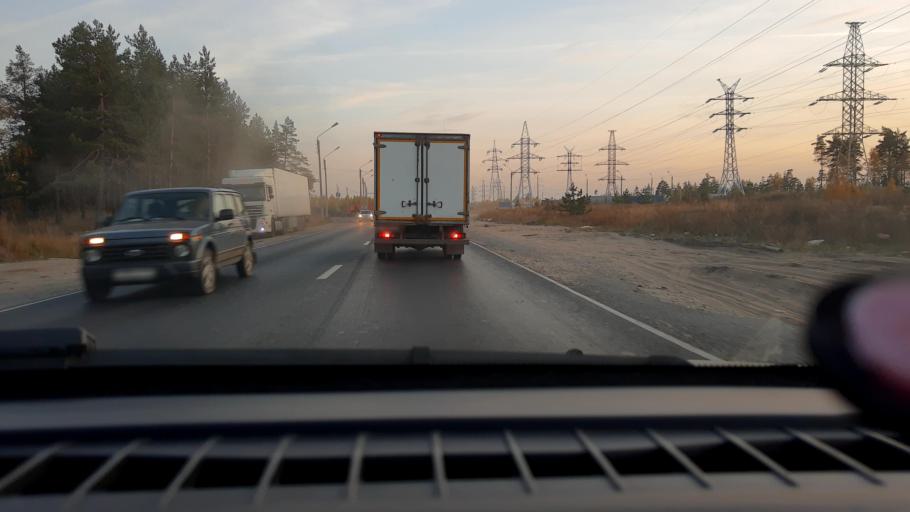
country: RU
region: Nizjnij Novgorod
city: Babino
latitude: 56.3039
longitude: 43.5591
